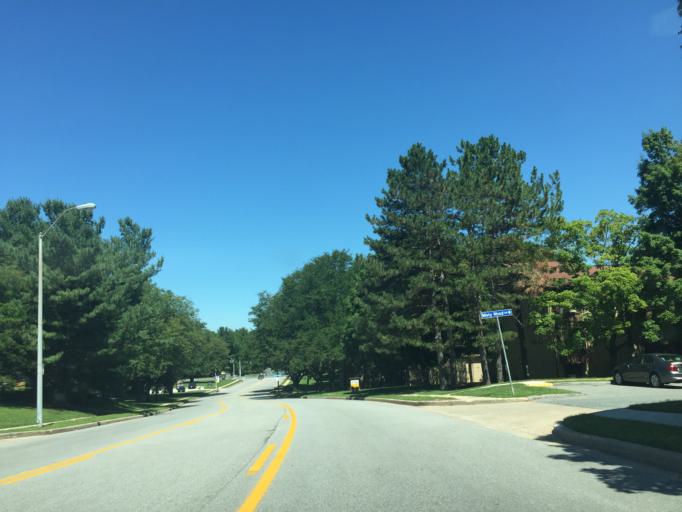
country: US
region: Maryland
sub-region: Baltimore County
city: Timonium
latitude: 39.4629
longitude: -76.6078
